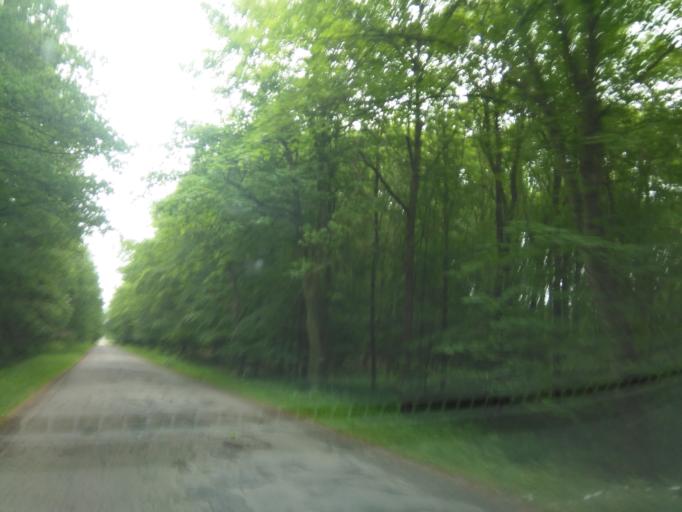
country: DK
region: Capital Region
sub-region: Bornholm Kommune
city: Akirkeby
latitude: 55.1114
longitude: 14.9346
